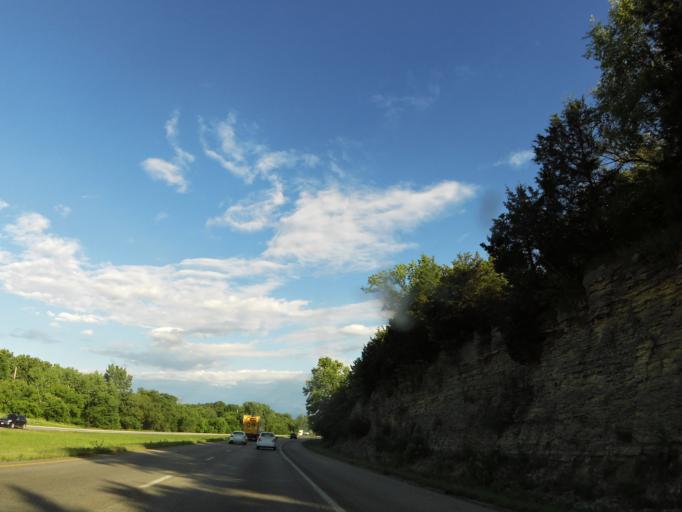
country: US
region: Missouri
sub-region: Saint Charles County
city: Wentzville
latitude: 38.8420
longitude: -90.8605
